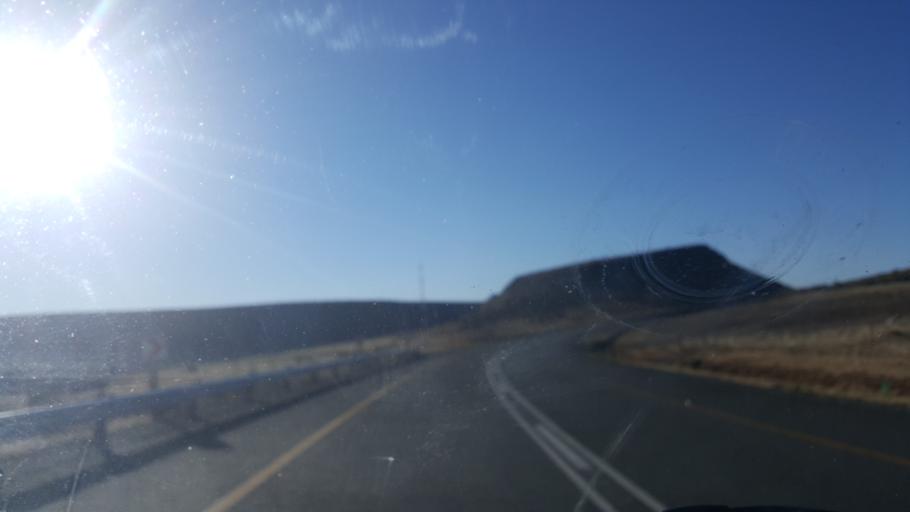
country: ZA
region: Eastern Cape
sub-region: Chris Hani District Municipality
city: Middelburg
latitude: -31.3751
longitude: 25.0313
